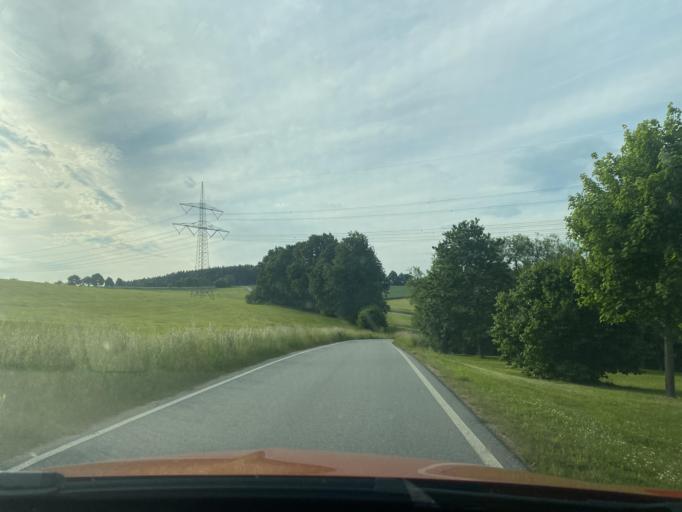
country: DE
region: Saxony
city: Bernstadt
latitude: 51.0305
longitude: 14.7999
